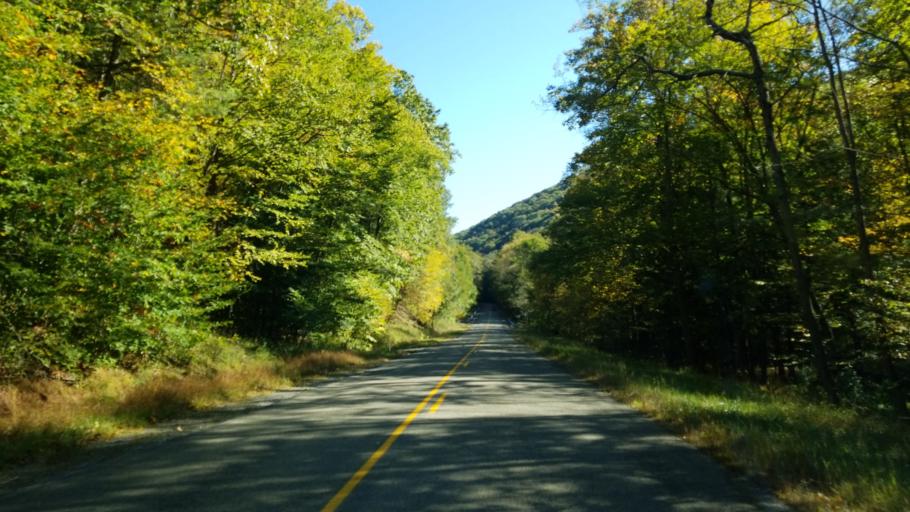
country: US
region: Pennsylvania
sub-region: Clearfield County
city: Clearfield
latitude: 41.2586
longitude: -78.3883
